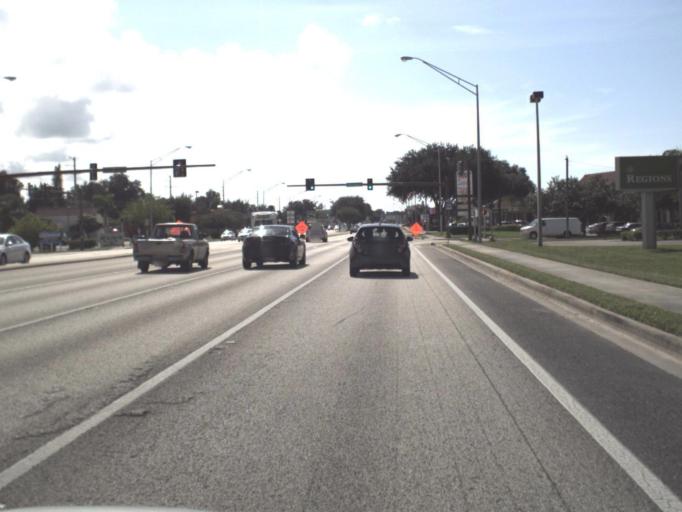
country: US
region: Florida
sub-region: Sarasota County
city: South Venice
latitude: 27.0570
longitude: -82.4129
